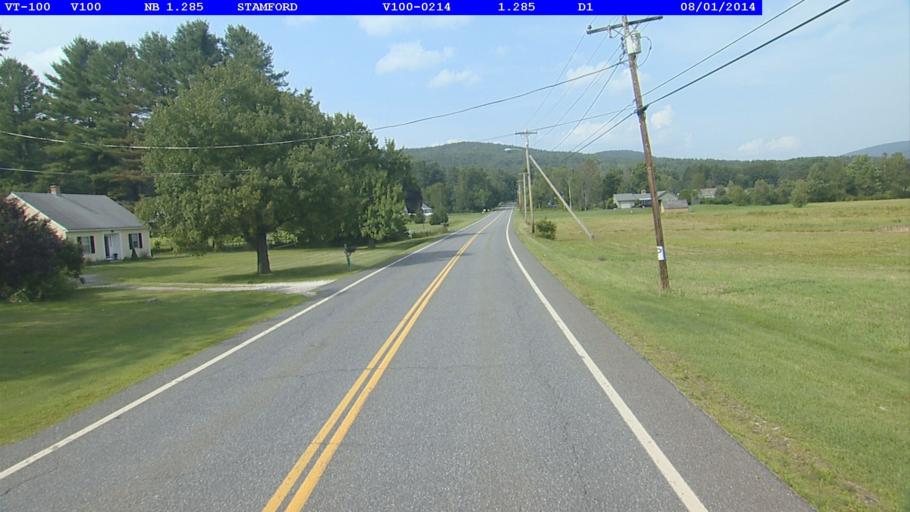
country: US
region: Massachusetts
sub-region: Berkshire County
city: North Adams
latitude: 42.7591
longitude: -73.0674
